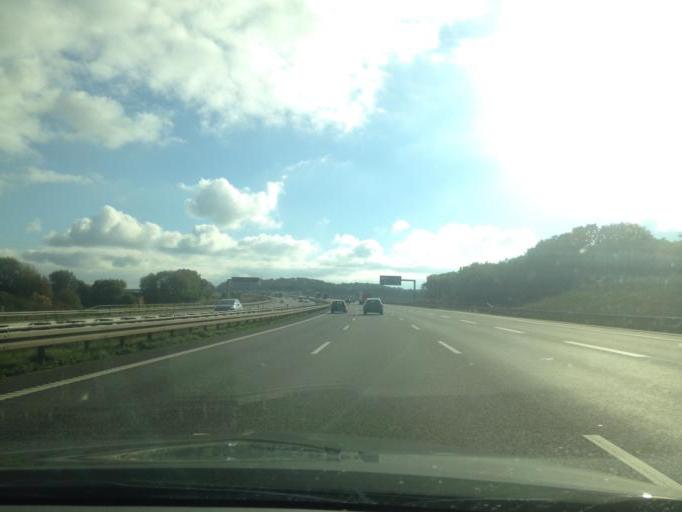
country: DK
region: South Denmark
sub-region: Vejle Kommune
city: Vejle
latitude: 55.6729
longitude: 9.5537
